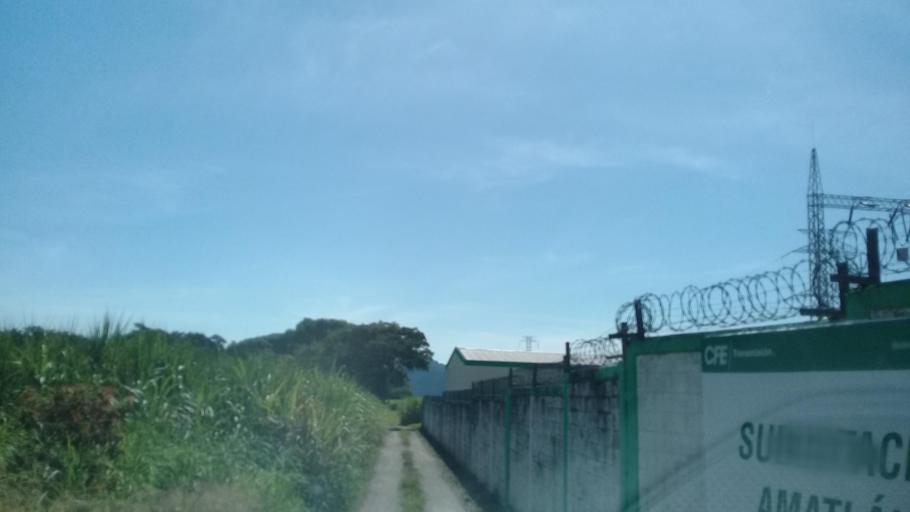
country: MX
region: Veracruz
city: Amatlan de los Reyes
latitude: 18.8586
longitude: -96.9019
